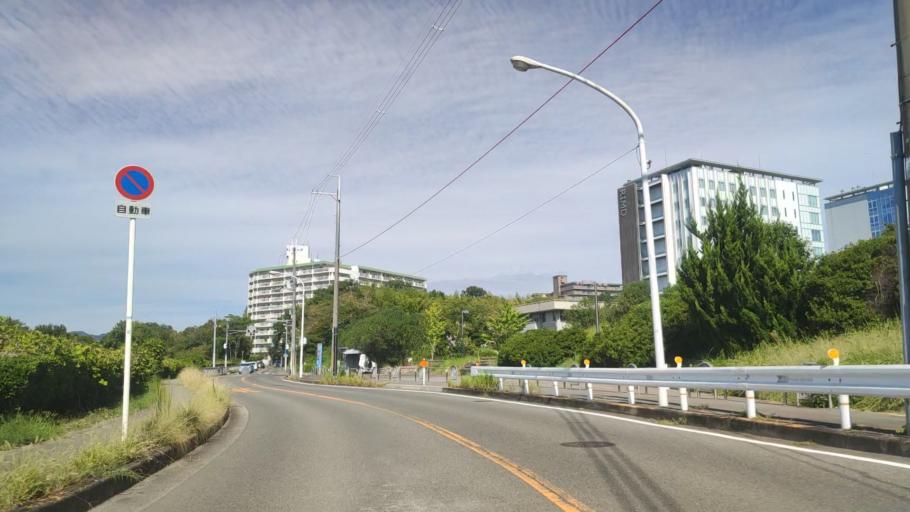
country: JP
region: Osaka
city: Ibaraki
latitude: 34.8223
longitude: 135.5200
